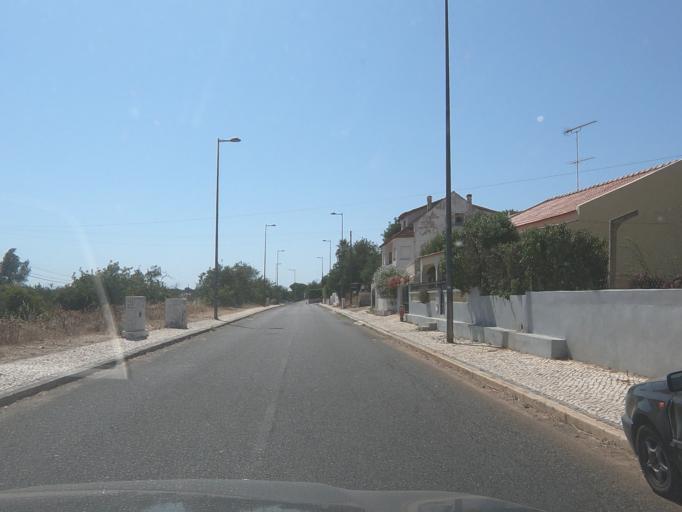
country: PT
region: Faro
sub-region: Faro
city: Santa Barbara de Nexe
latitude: 37.0914
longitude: -7.9822
